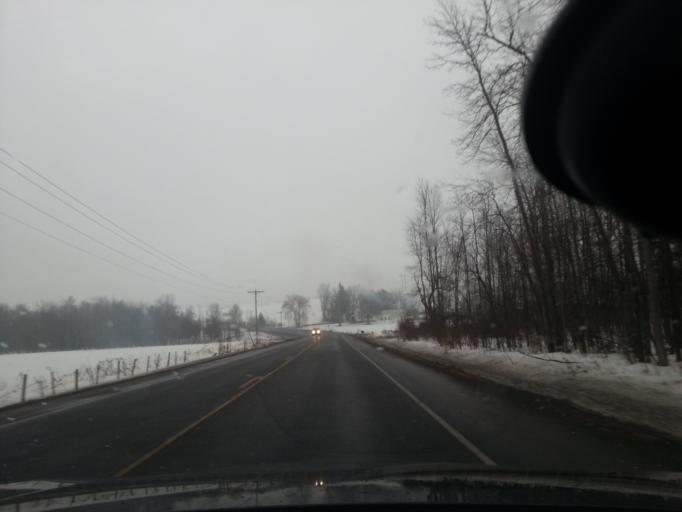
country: US
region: New York
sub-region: St. Lawrence County
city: Ogdensburg
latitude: 44.5962
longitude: -75.3828
